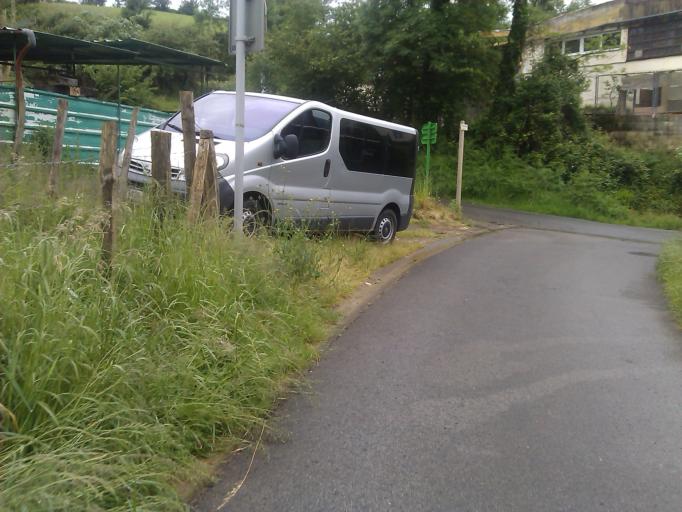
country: ES
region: Basque Country
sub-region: Provincia de Guipuzcoa
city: Urnieta
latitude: 43.2524
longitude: -1.9832
